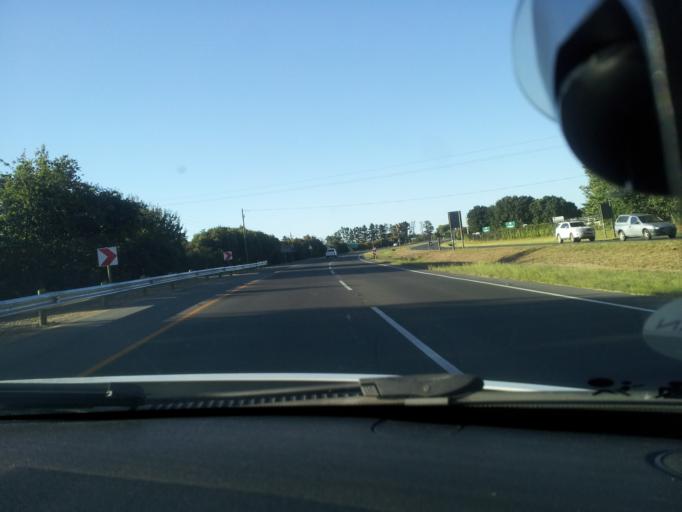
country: ZA
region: Western Cape
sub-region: Cape Winelands District Municipality
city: Stellenbosch
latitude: -34.0286
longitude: 18.8207
